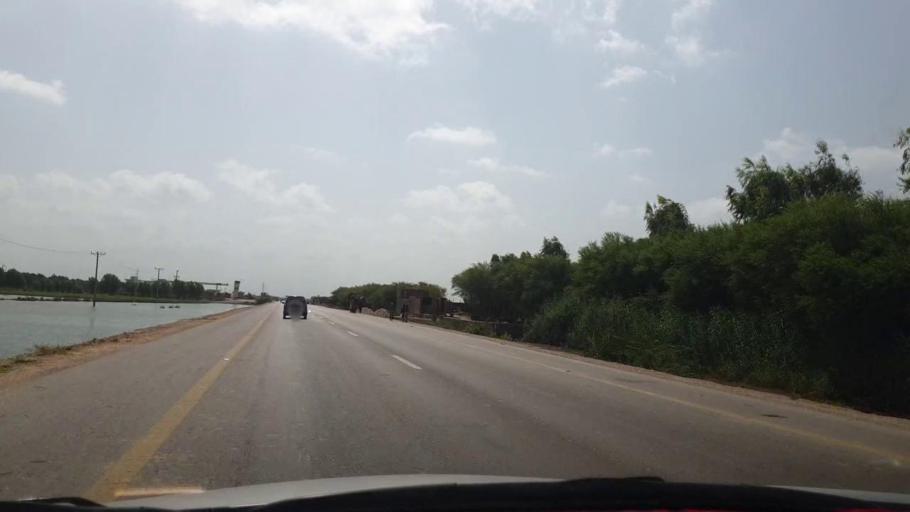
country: PK
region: Sindh
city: Talhar
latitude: 24.9326
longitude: 68.7116
